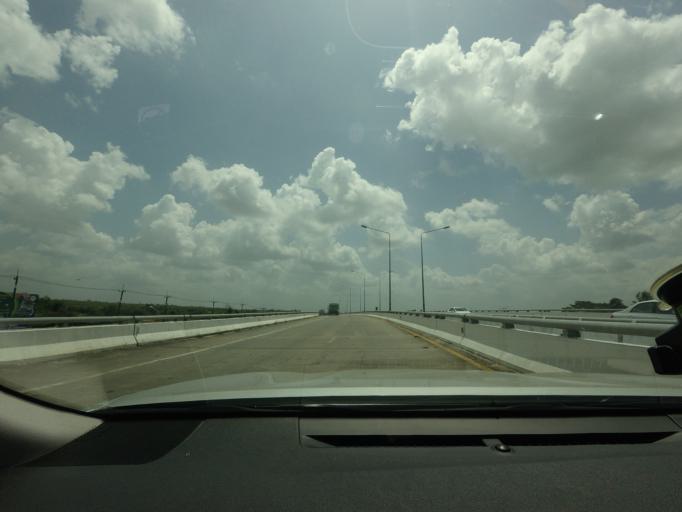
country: TH
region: Nakhon Si Thammarat
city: Phra Phrom
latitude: 8.3428
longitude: 99.9265
